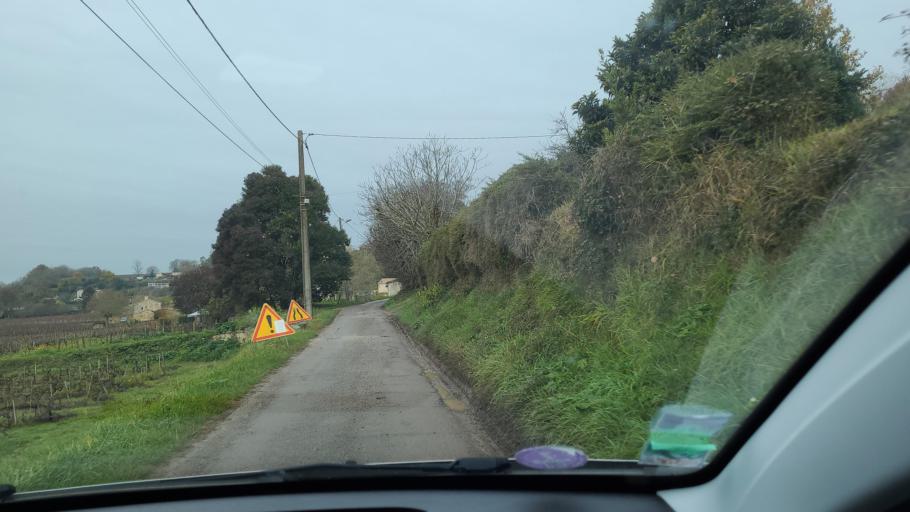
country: FR
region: Aquitaine
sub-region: Departement de la Gironde
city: Bourg
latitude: 45.0425
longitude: -0.5700
